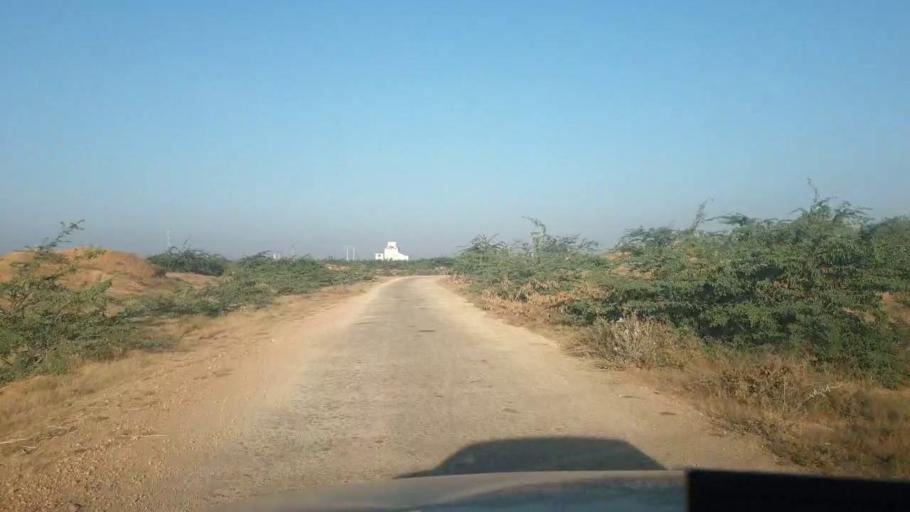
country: PK
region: Sindh
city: Thatta
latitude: 24.6981
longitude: 67.8582
